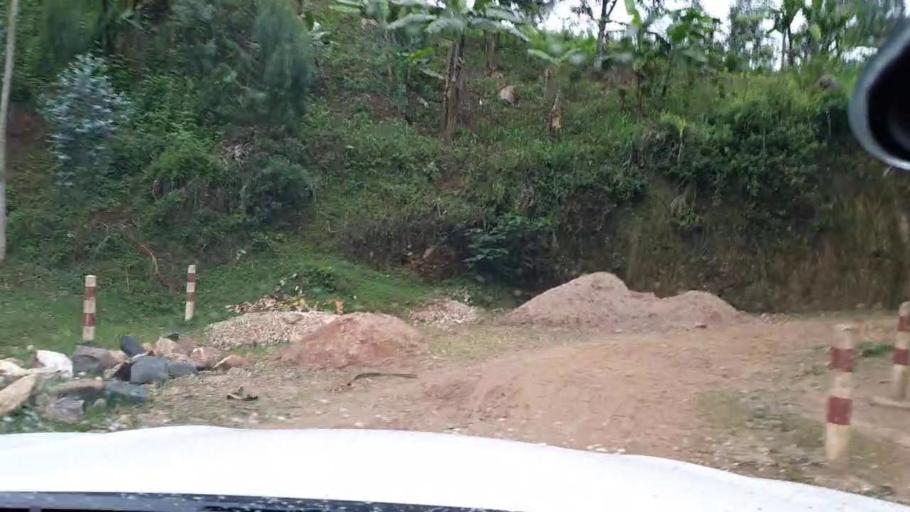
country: RW
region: Southern Province
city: Nzega
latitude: -2.3990
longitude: 29.2318
